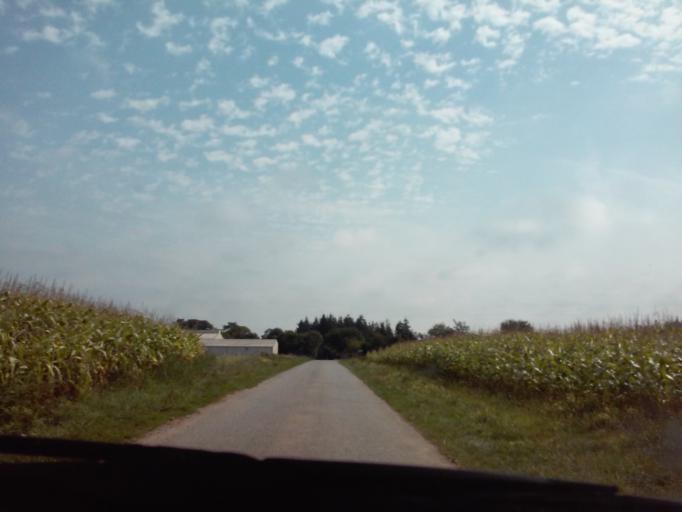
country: FR
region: Brittany
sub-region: Departement du Morbihan
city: Ploermel
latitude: 47.9043
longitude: -2.3922
